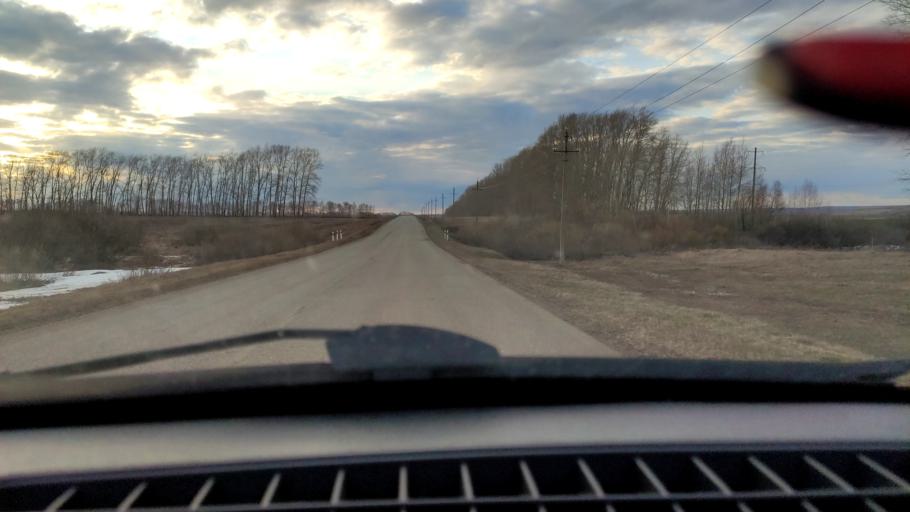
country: RU
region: Bashkortostan
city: Tolbazy
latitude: 53.9930
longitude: 55.7819
